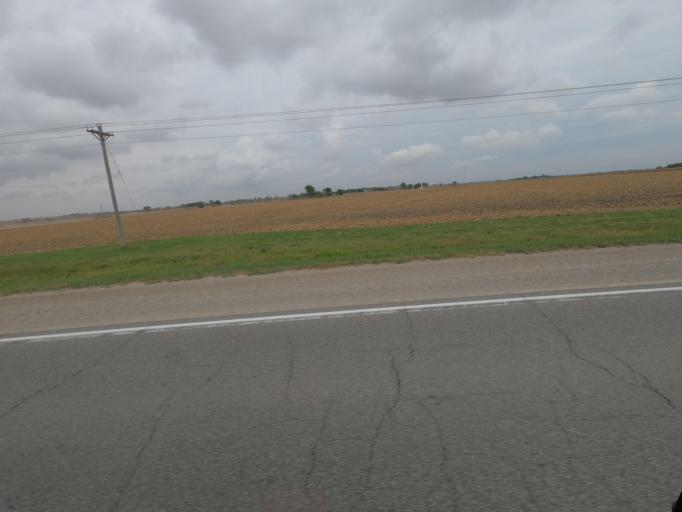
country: US
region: Iowa
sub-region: Wapello County
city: Ottumwa
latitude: 40.9483
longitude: -92.2272
